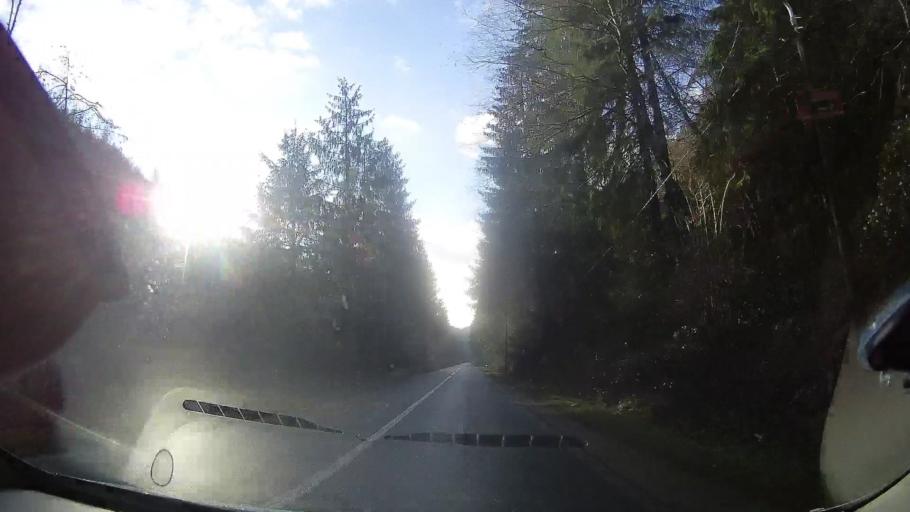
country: RO
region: Alba
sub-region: Comuna Albac
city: Albac
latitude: 46.4382
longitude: 22.9672
